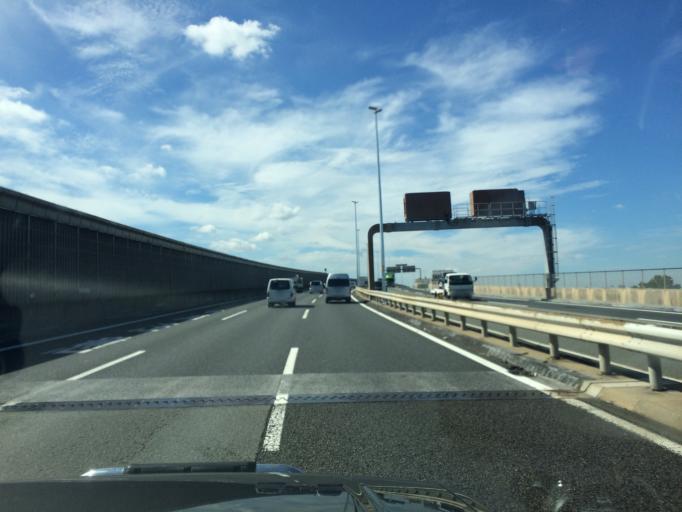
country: JP
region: Osaka
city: Matsubara
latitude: 34.5459
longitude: 135.5596
